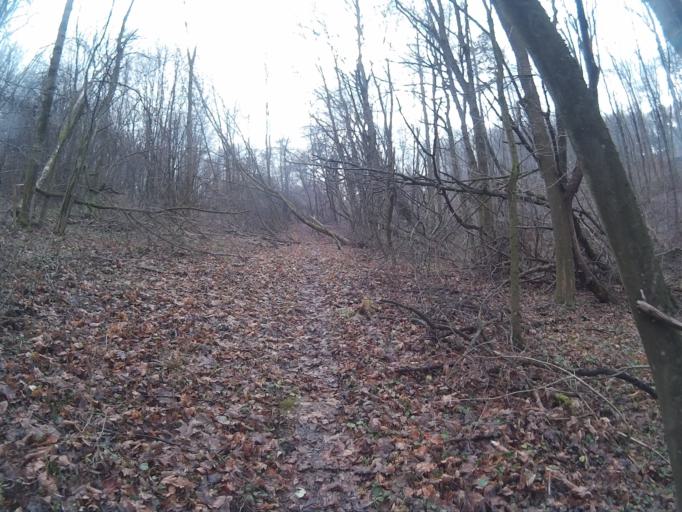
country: HU
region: Veszprem
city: Urkut
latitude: 47.1363
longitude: 17.6503
